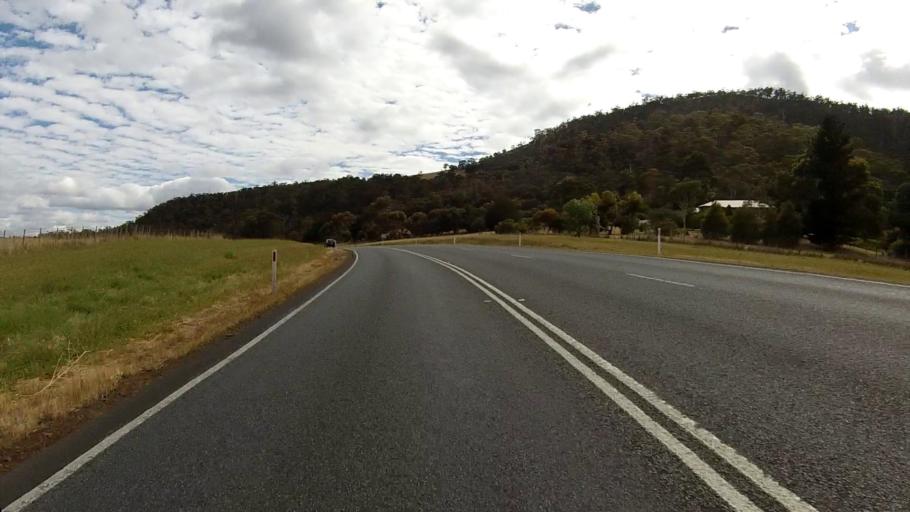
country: AU
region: Tasmania
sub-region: Brighton
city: Old Beach
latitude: -42.7943
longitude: 147.2923
